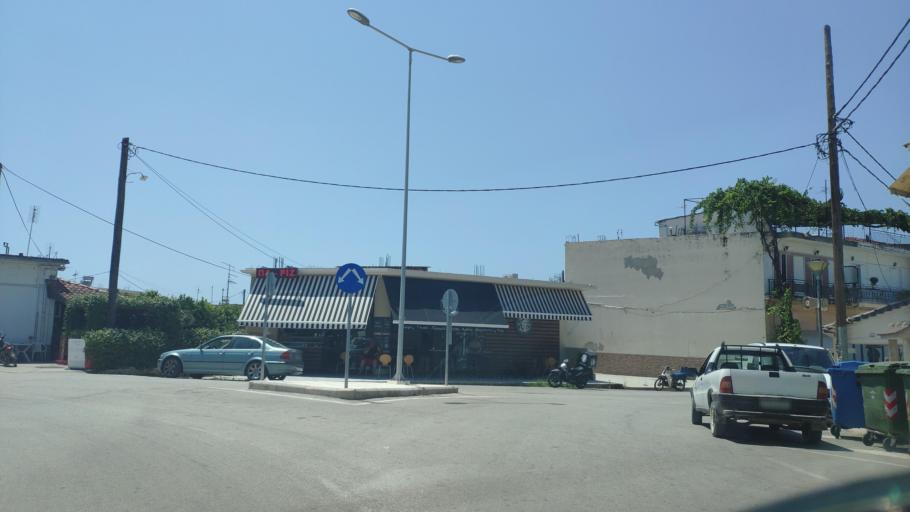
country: GR
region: Epirus
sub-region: Nomos Artas
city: Neochori
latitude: 39.0711
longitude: 21.0220
